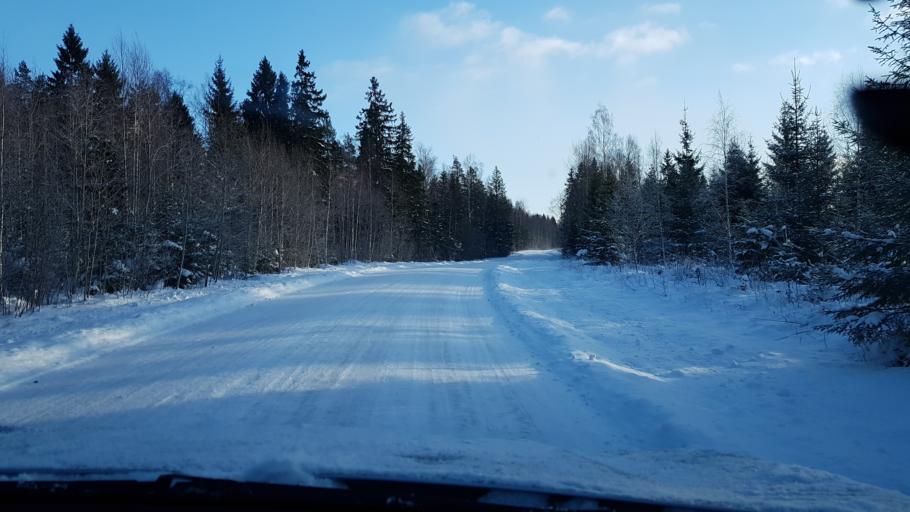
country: EE
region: Harju
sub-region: Nissi vald
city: Turba
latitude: 59.1359
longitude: 24.1901
